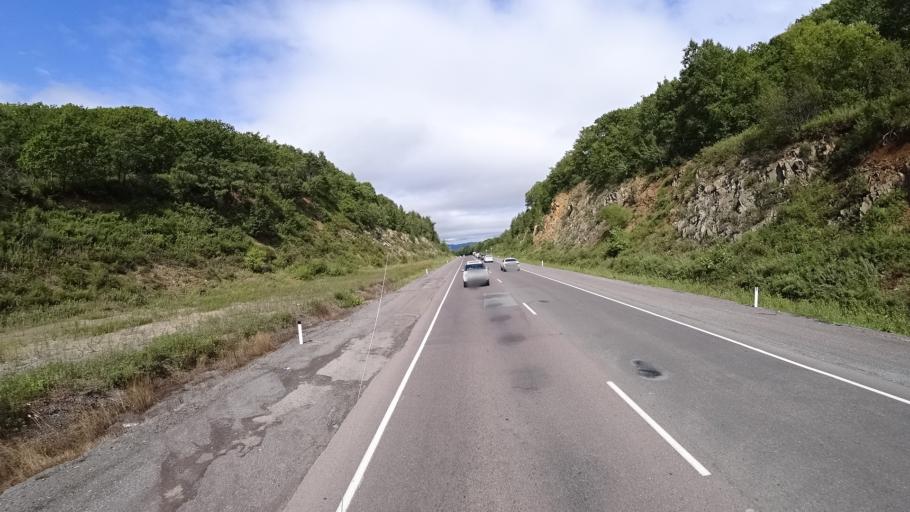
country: RU
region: Primorskiy
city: Lyalichi
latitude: 44.1276
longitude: 132.4252
